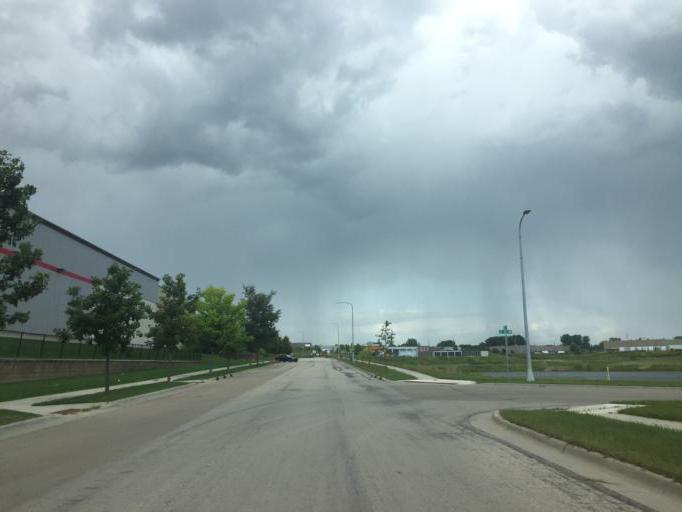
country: US
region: Minnesota
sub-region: Olmsted County
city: Rochester
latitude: 44.0469
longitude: -92.5161
